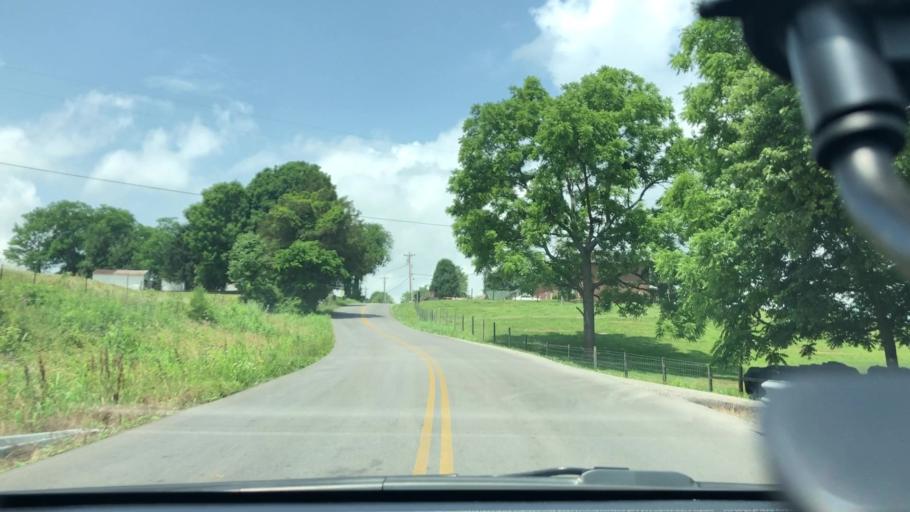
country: US
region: Kentucky
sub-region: Pulaski County
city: Somerset
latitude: 37.0594
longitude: -84.6645
